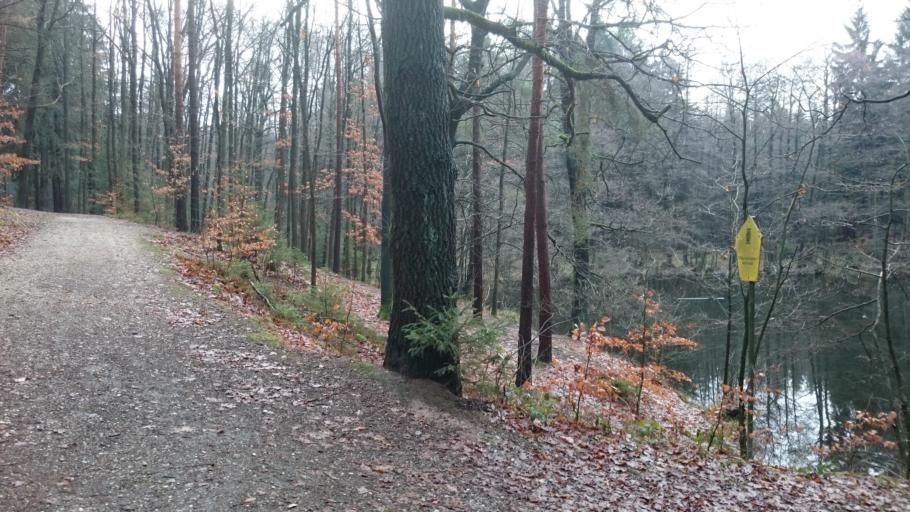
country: DE
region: Saxony
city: Mulsen
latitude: 50.7876
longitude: 12.5746
